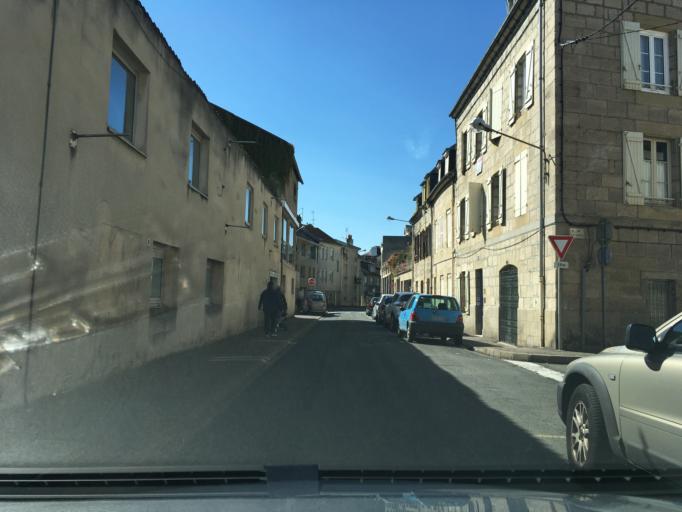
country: FR
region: Limousin
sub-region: Departement de la Correze
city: Brive-la-Gaillarde
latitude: 45.1620
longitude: 1.5309
